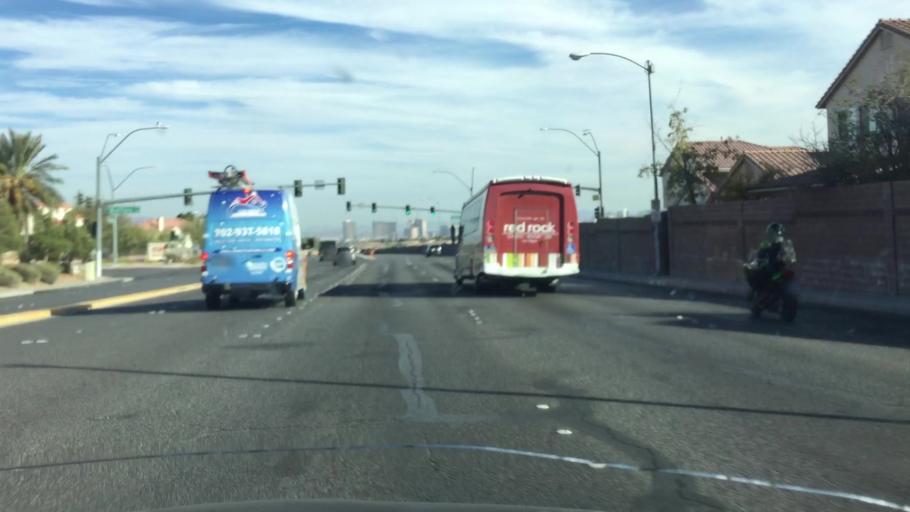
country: US
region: Nevada
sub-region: Clark County
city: Spring Valley
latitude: 36.1291
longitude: -115.2619
